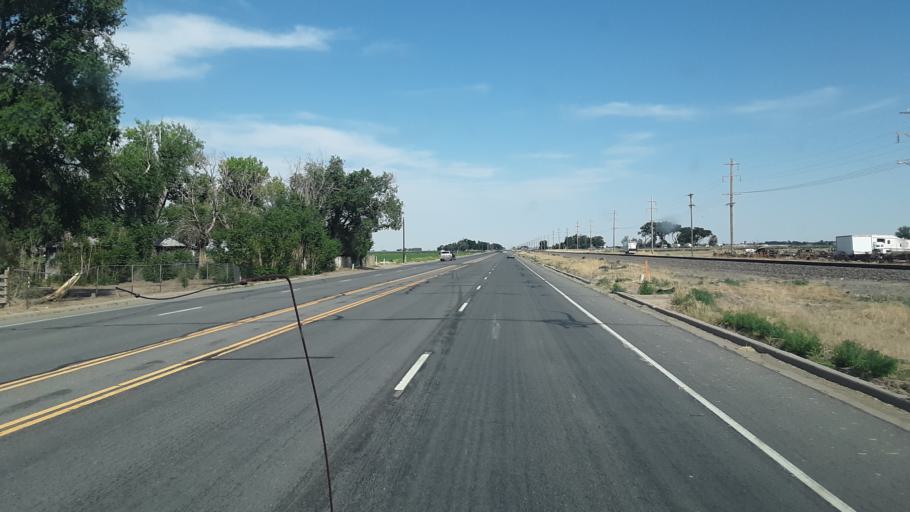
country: US
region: Colorado
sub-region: Otero County
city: Rocky Ford
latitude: 38.0982
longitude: -103.8321
